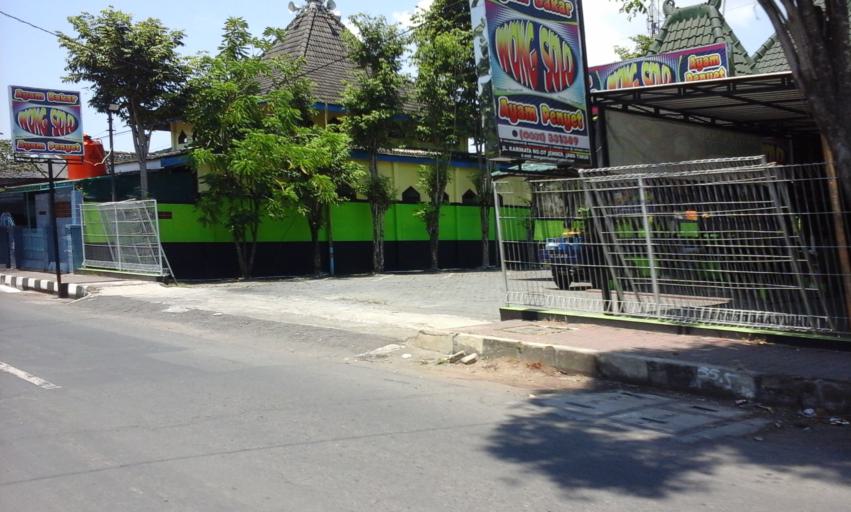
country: ID
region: East Java
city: Sumbersari Wetan
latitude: -8.1803
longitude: 113.7159
